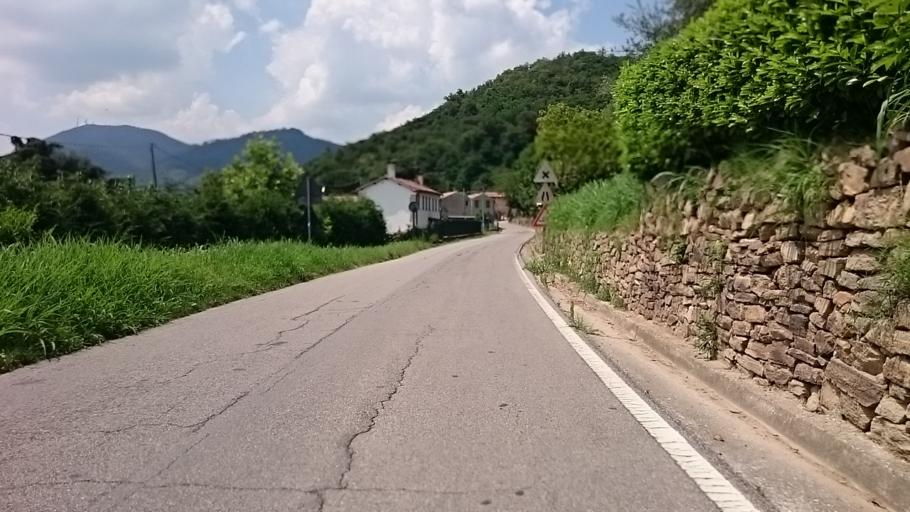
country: IT
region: Veneto
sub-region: Provincia di Padova
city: Galzignano
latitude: 45.3088
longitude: 11.7491
